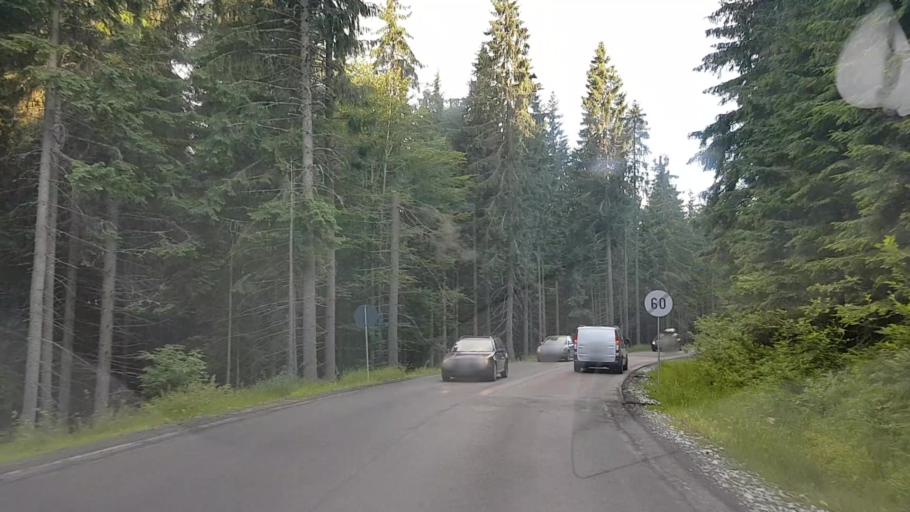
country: RO
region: Harghita
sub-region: Comuna Varsag
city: Varsag
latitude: 46.6610
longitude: 25.3014
